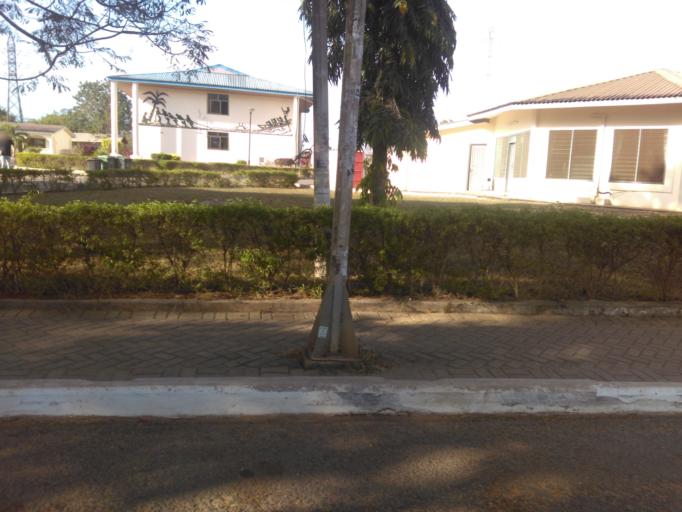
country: GH
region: Central
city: Cape Coast
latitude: 5.1182
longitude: -1.2900
